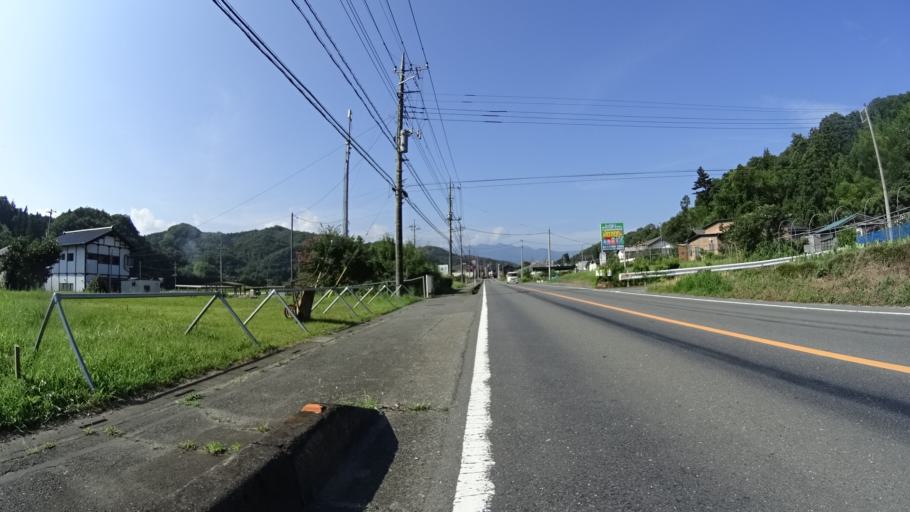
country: JP
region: Saitama
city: Chichibu
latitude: 36.0234
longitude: 139.0678
